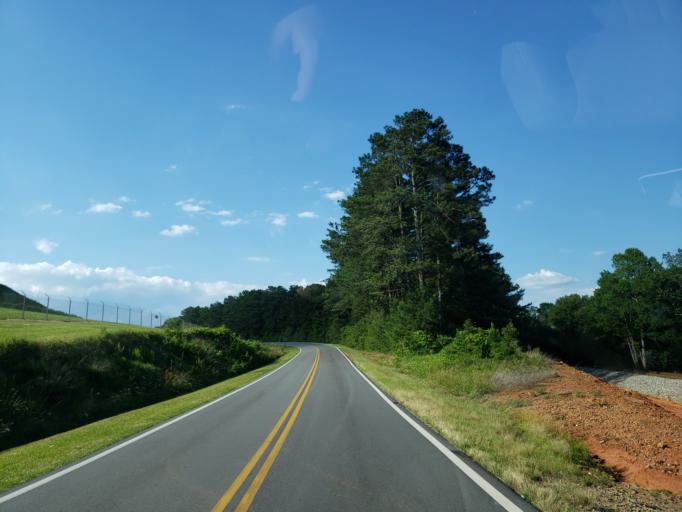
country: US
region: Georgia
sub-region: Haralson County
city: Bremen
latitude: 33.6932
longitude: -85.1359
